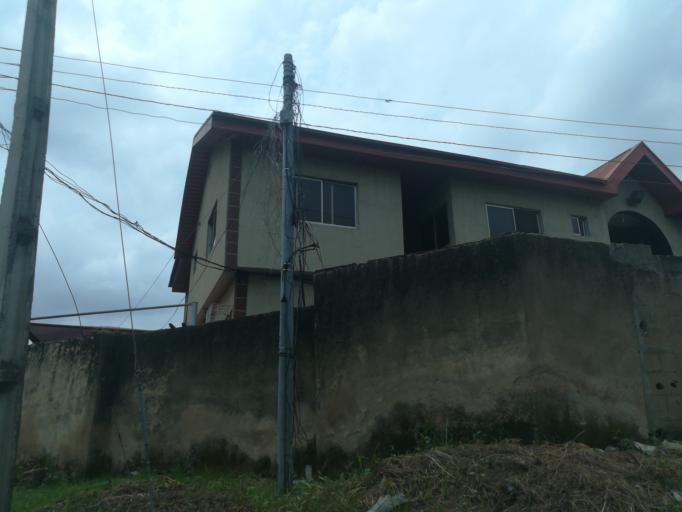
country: NG
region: Lagos
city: Ojota
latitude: 6.5910
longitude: 3.3648
